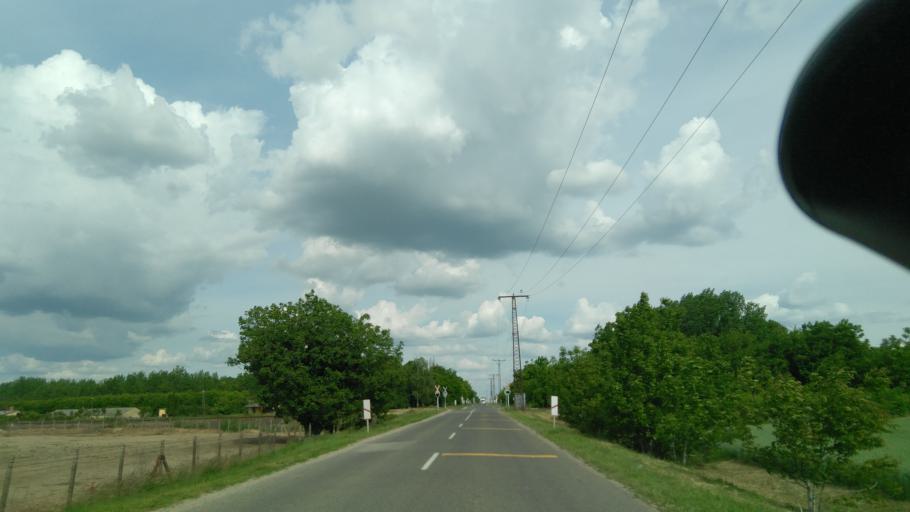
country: HU
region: Bekes
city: Mezohegyes
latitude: 46.3158
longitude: 20.8295
